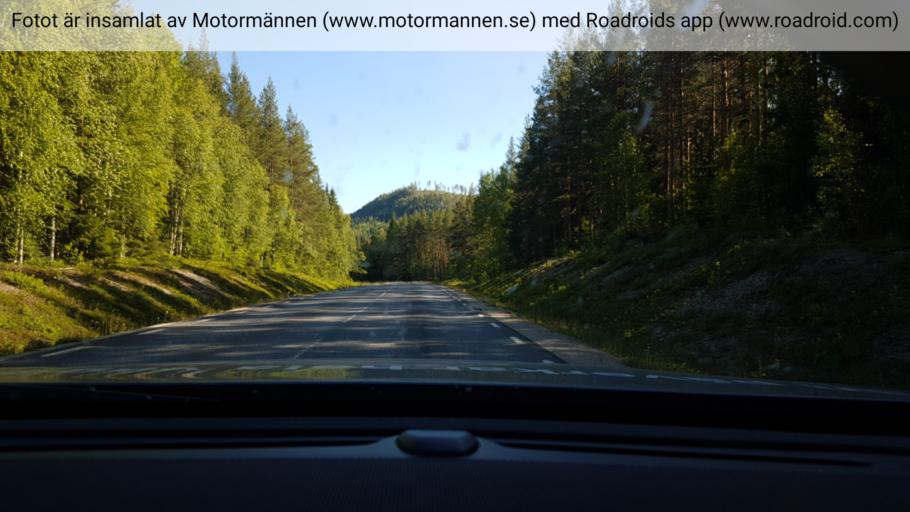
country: SE
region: Vaesterbotten
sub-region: Lycksele Kommun
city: Lycksele
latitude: 64.4215
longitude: 19.0050
